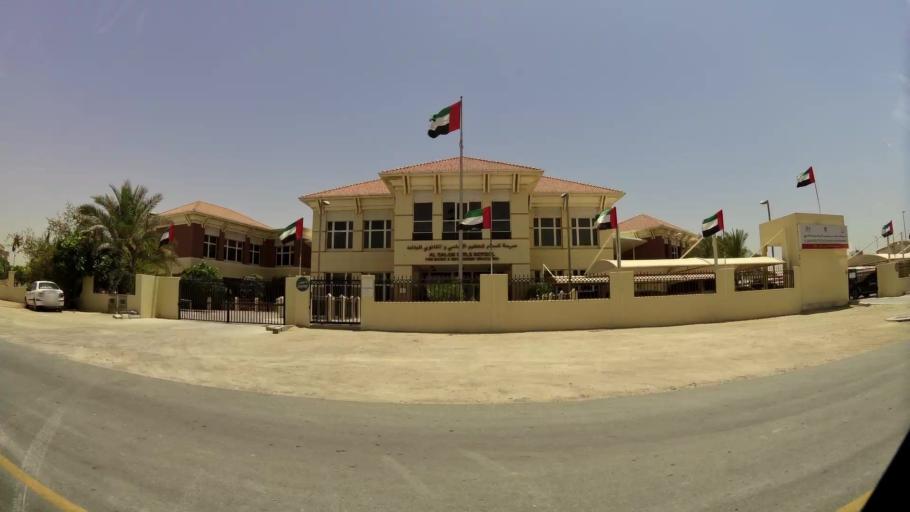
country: AE
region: Dubai
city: Dubai
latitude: 25.0940
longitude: 55.1977
